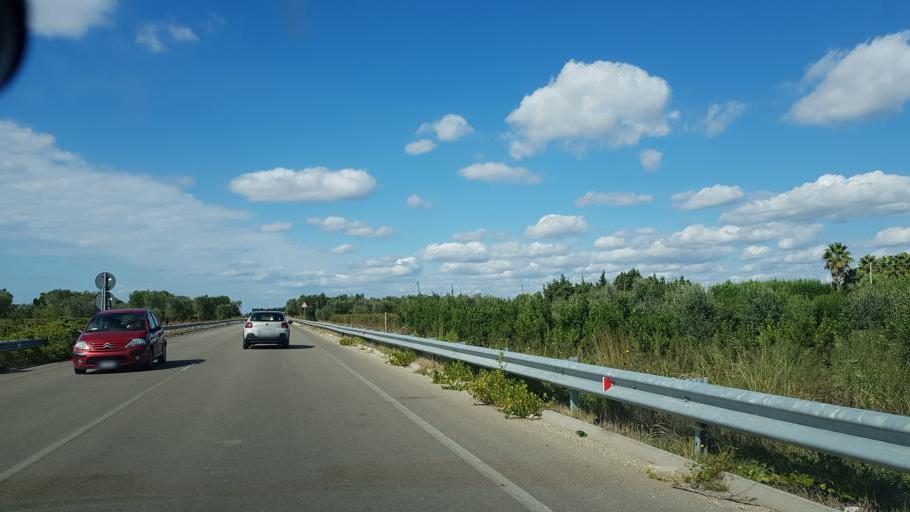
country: IT
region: Apulia
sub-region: Provincia di Lecce
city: Leverano
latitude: 40.3057
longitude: 17.9981
